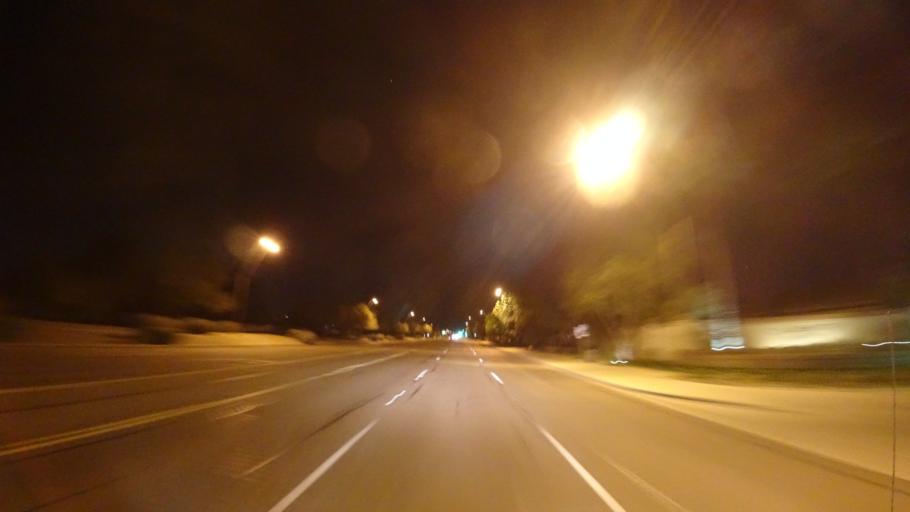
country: US
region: Arizona
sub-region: Maricopa County
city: Guadalupe
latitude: 33.3463
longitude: -111.9285
